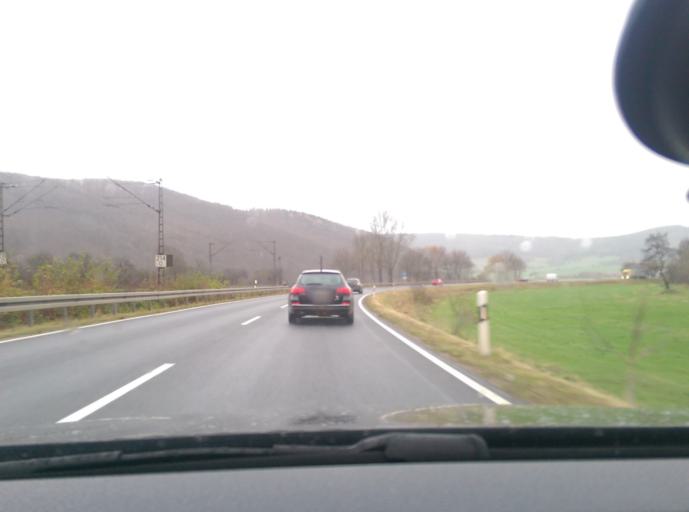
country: DE
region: Hesse
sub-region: Regierungsbezirk Kassel
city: Bad Sooden-Allendorf
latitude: 51.2807
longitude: 9.9631
